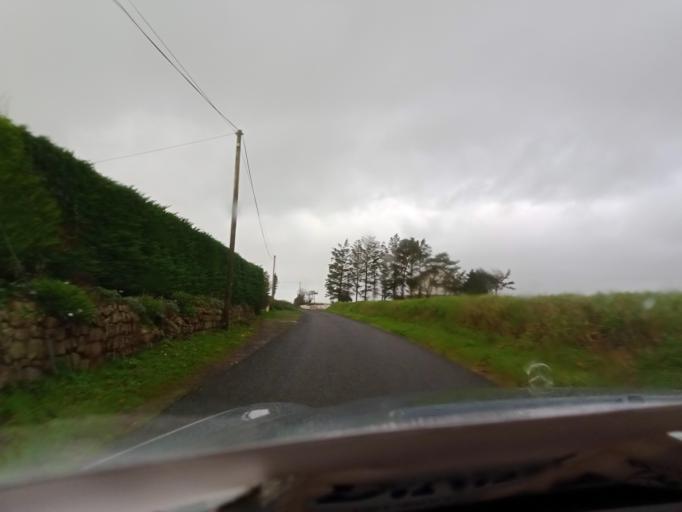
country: IE
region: Leinster
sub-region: Kilkenny
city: Mooncoin
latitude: 52.2716
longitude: -7.1860
